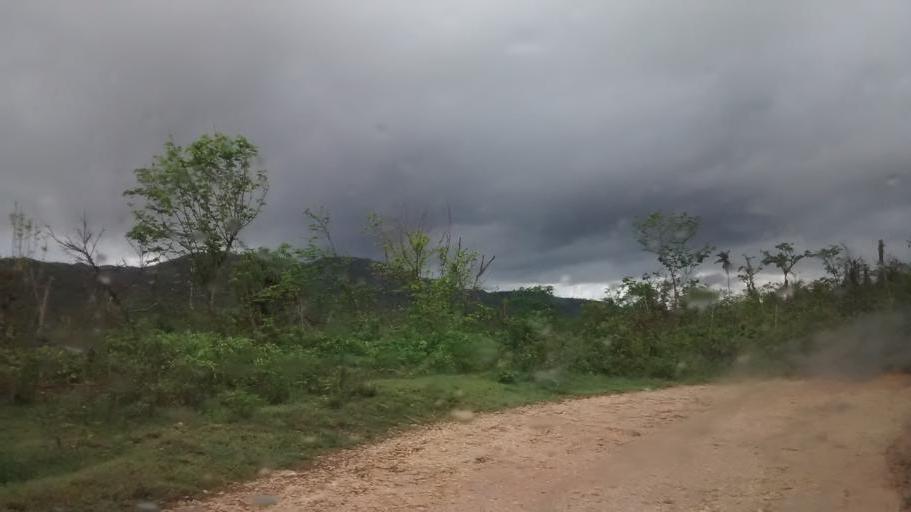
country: HT
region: Grandans
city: Corail
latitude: 18.5375
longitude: -73.9861
